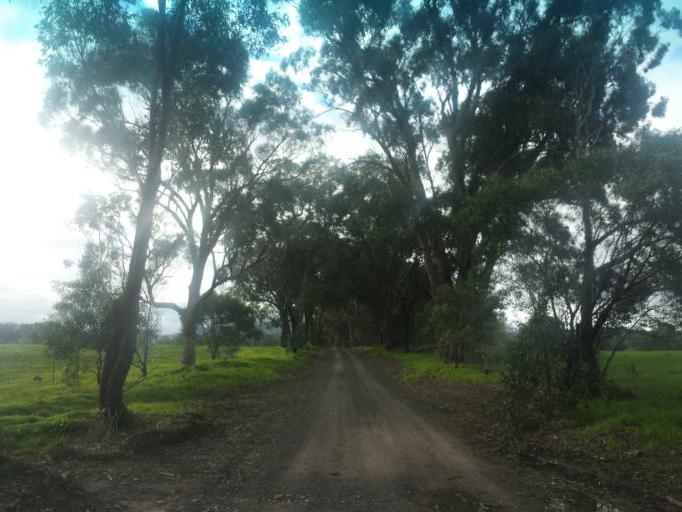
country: AU
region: Victoria
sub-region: Murrindindi
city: Kinglake West
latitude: -37.0440
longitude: 145.2502
